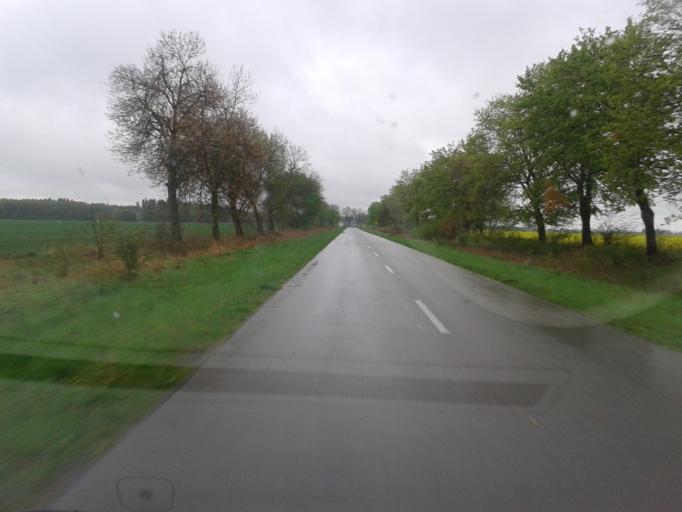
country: UA
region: Lviv
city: Uhniv
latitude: 50.4169
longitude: 23.7533
